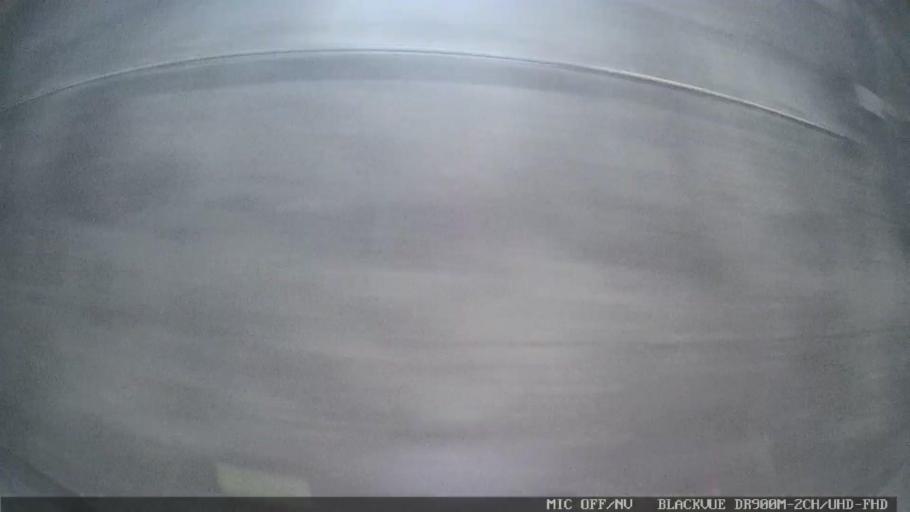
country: BR
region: Sao Paulo
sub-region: Cubatao
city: Cubatao
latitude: -23.8807
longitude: -46.4867
